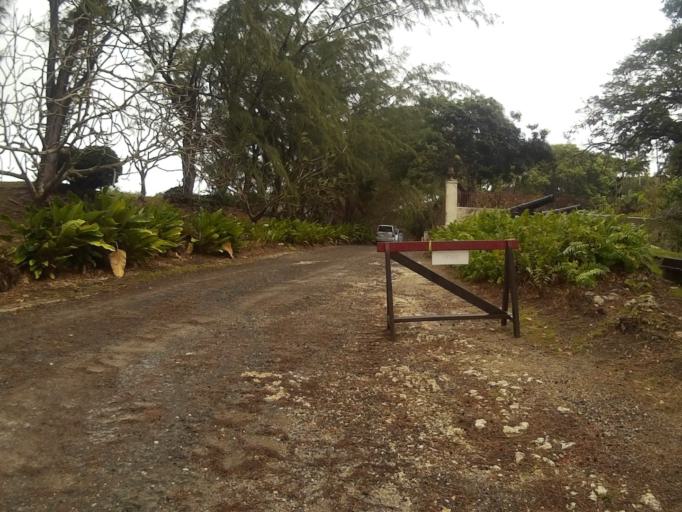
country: BB
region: Saint Andrew
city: Greenland
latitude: 13.2777
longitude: -59.5891
